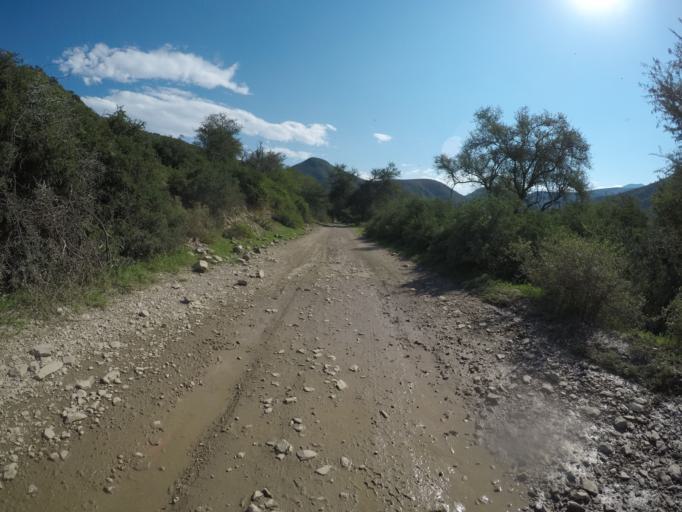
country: ZA
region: Eastern Cape
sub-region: Cacadu District Municipality
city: Kareedouw
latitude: -33.6654
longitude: 24.3738
